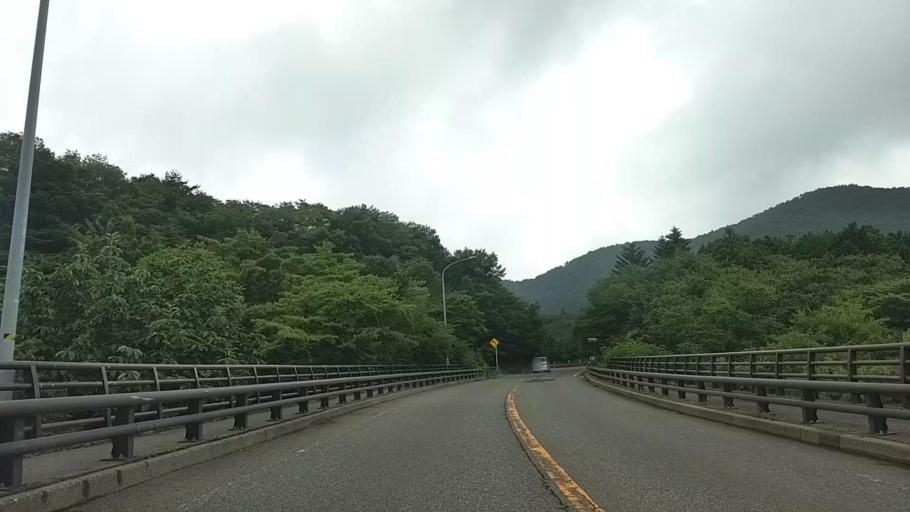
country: JP
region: Yamanashi
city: Fujikawaguchiko
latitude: 35.4534
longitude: 138.6088
